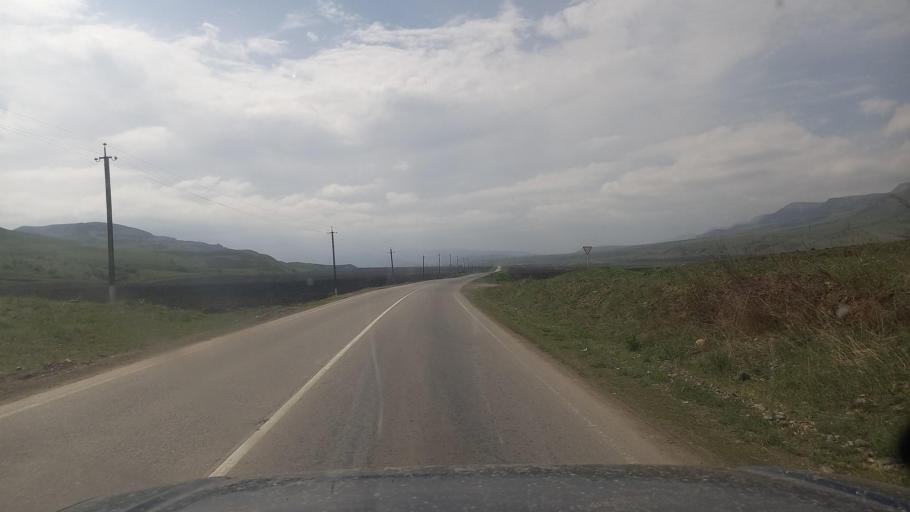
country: RU
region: Kabardino-Balkariya
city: Kamennomostskoye
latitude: 43.7239
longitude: 43.1241
